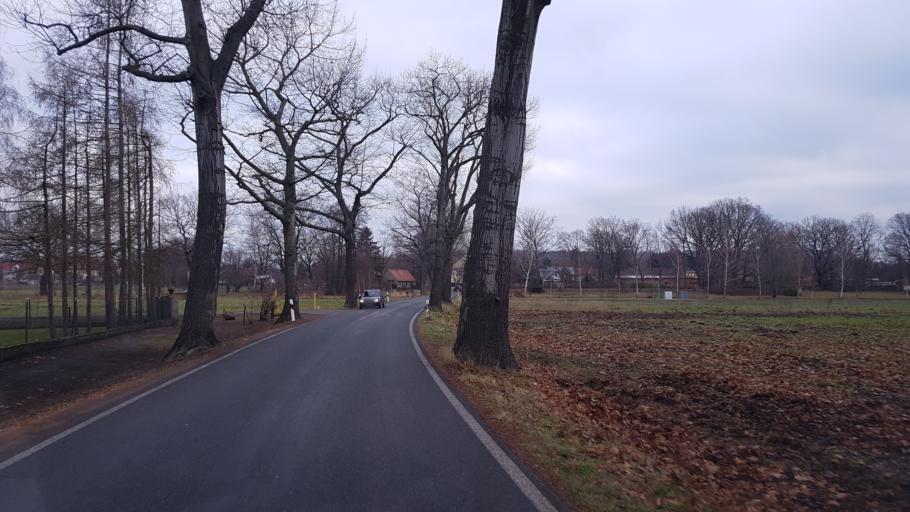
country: DE
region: Brandenburg
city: Schipkau
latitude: 51.5559
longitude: 13.8931
